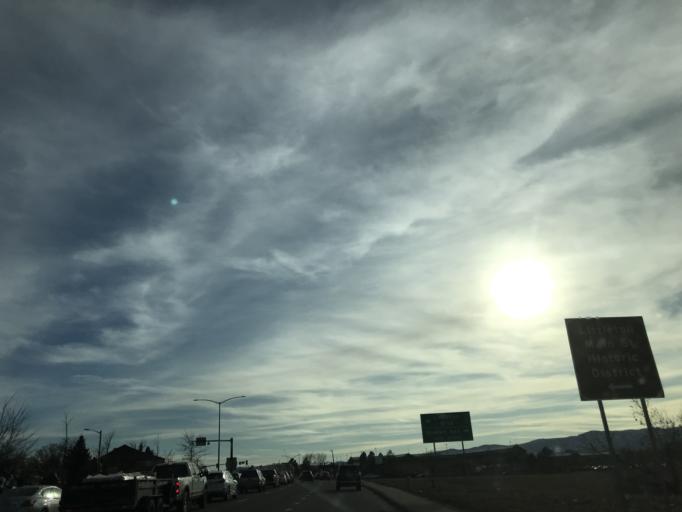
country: US
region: Colorado
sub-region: Arapahoe County
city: Littleton
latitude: 39.6152
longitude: -105.0203
